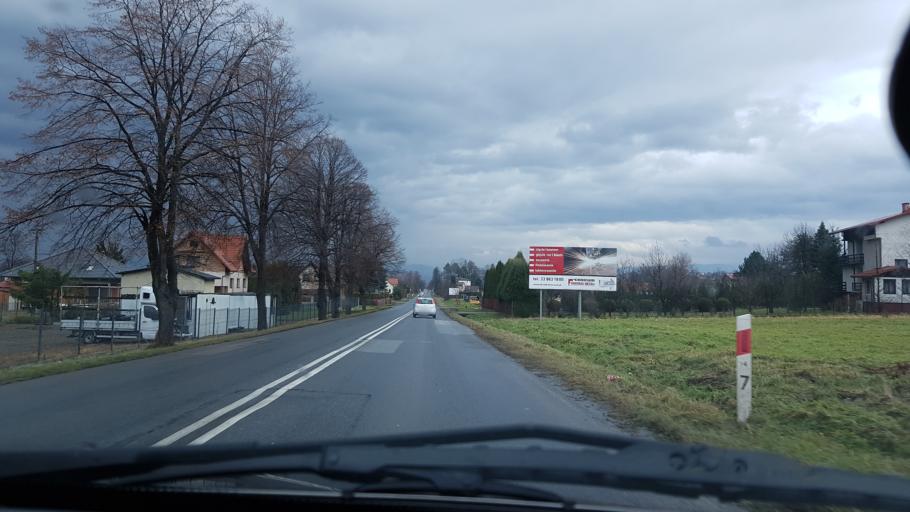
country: PL
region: Silesian Voivodeship
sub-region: Powiat zywiecki
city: Lodygowice
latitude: 49.7184
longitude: 19.1513
